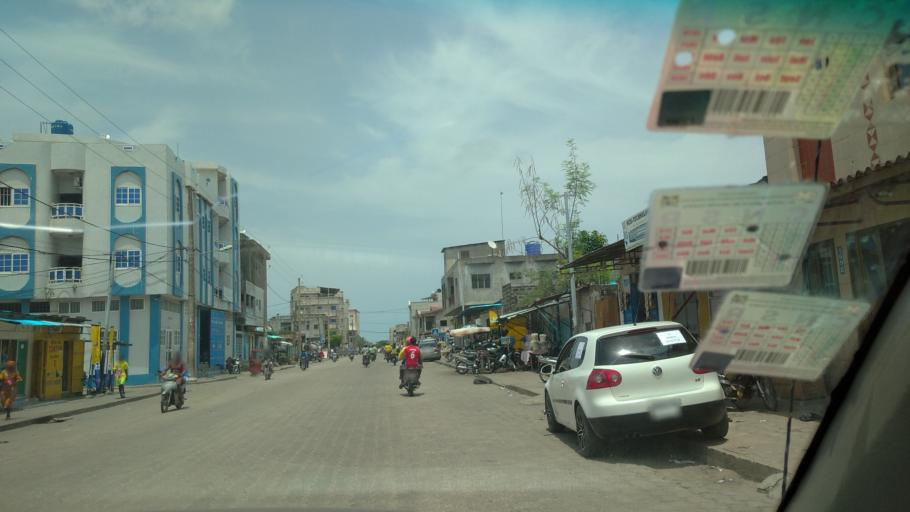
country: BJ
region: Littoral
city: Cotonou
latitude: 6.3920
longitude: 2.4536
